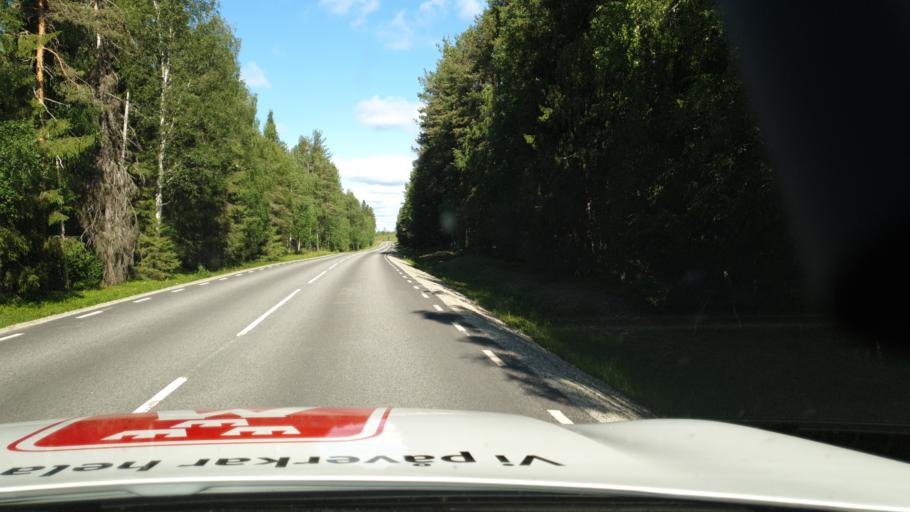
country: SE
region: Vaesterbotten
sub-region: Norsjo Kommun
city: Norsjoe
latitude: 64.7404
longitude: 19.1154
